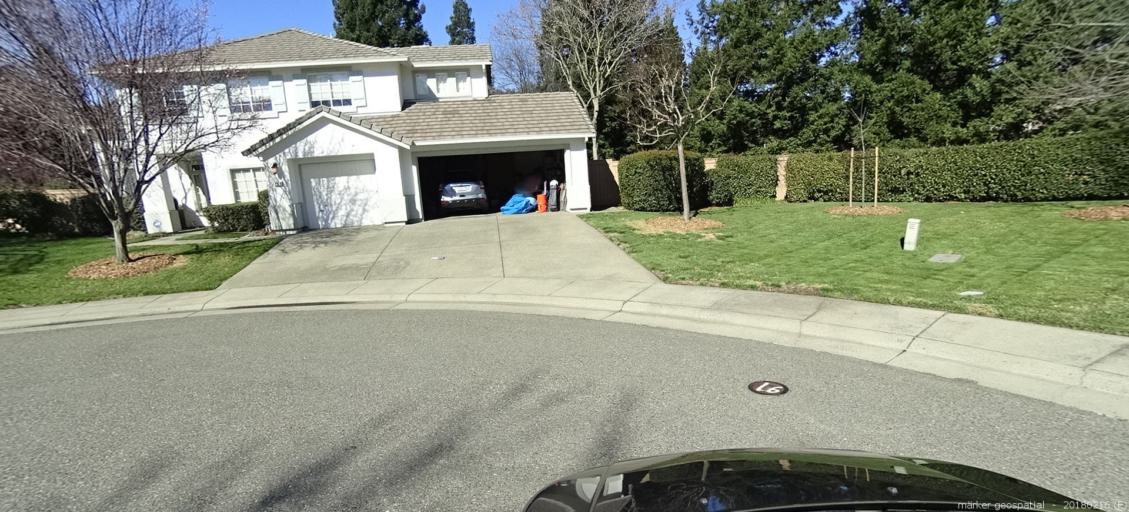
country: US
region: California
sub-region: Sacramento County
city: Gold River
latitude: 38.6224
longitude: -121.2433
